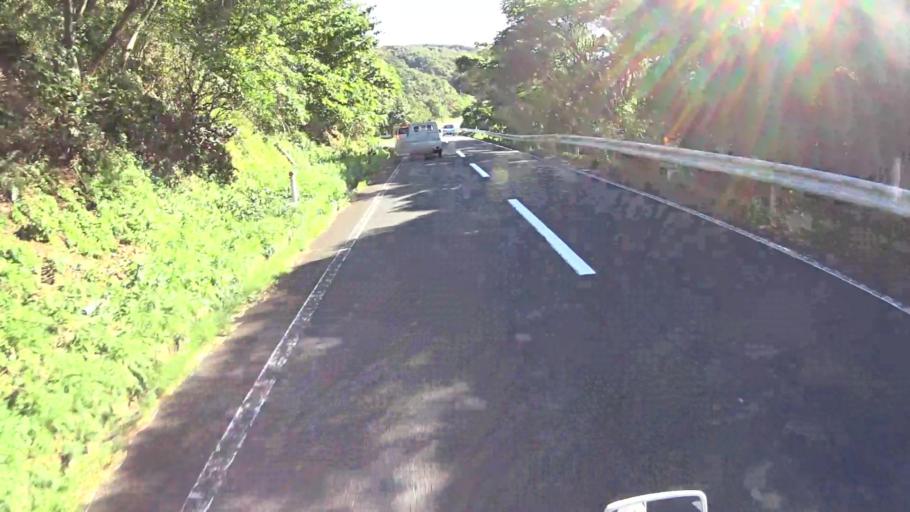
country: JP
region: Kyoto
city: Miyazu
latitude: 35.7126
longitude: 135.0690
